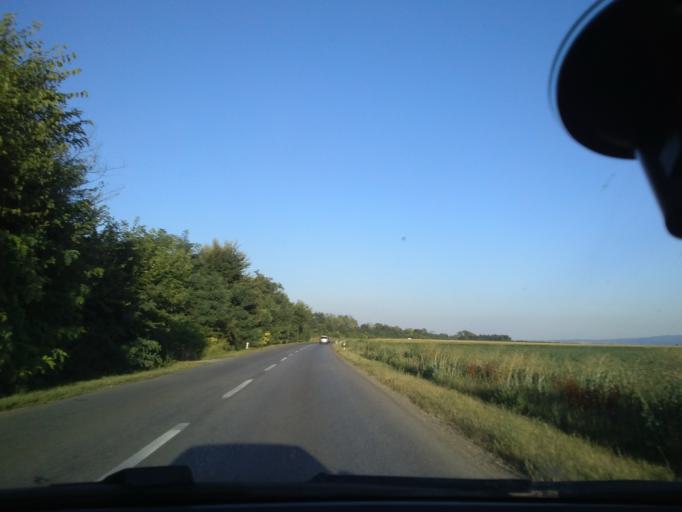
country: RS
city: Kisac
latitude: 45.3338
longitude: 19.6776
